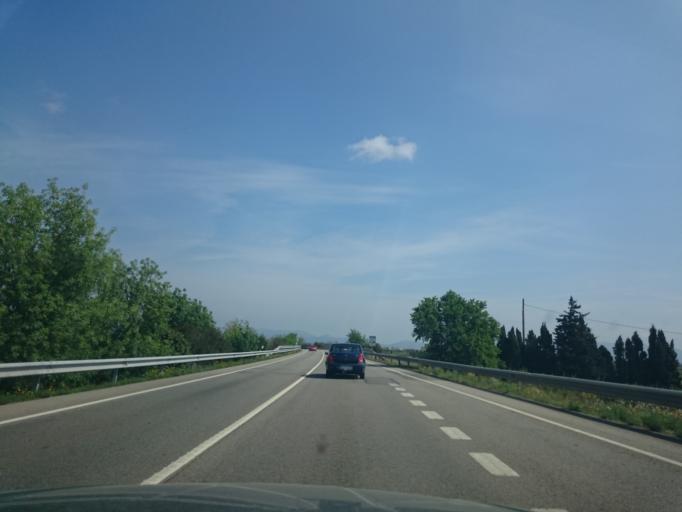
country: ES
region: Catalonia
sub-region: Provincia de Girona
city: Vilamalla
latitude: 42.2356
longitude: 2.9808
